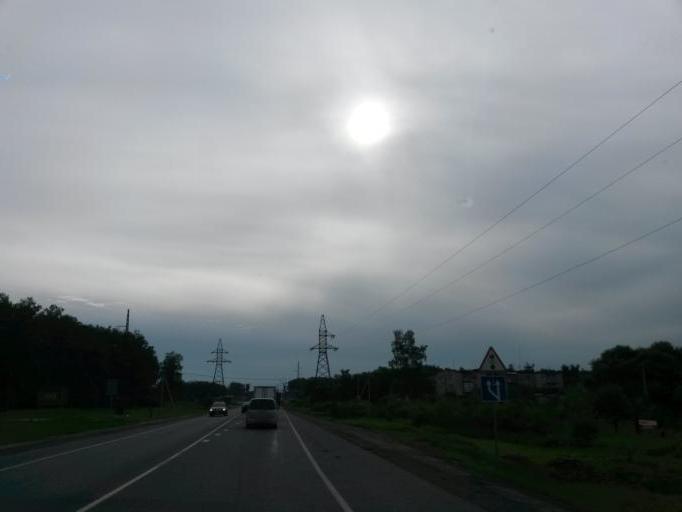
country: RU
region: Moskovskaya
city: Belyye Stolby
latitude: 55.3379
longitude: 37.7968
